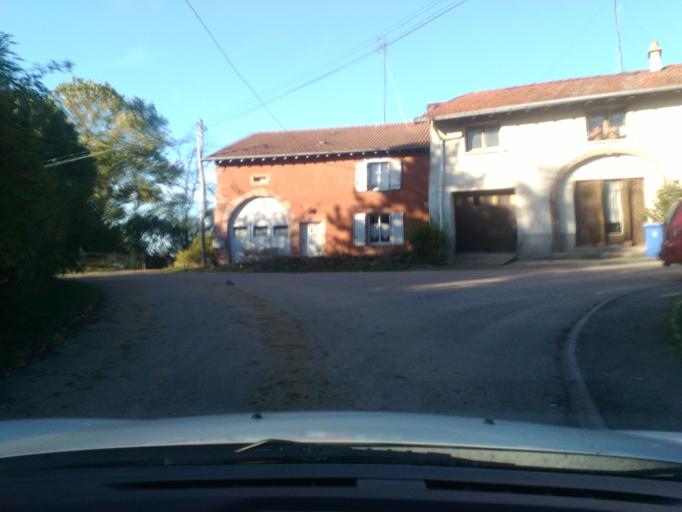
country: FR
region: Lorraine
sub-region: Departement des Vosges
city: Jeanmenil
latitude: 48.2925
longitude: 6.7101
